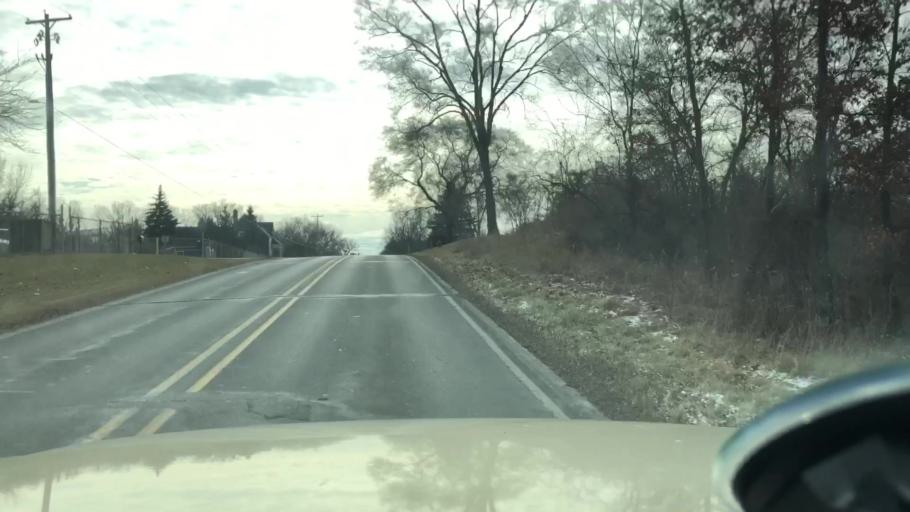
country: US
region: Michigan
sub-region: Jackson County
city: Jackson
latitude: 42.2741
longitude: -84.3650
